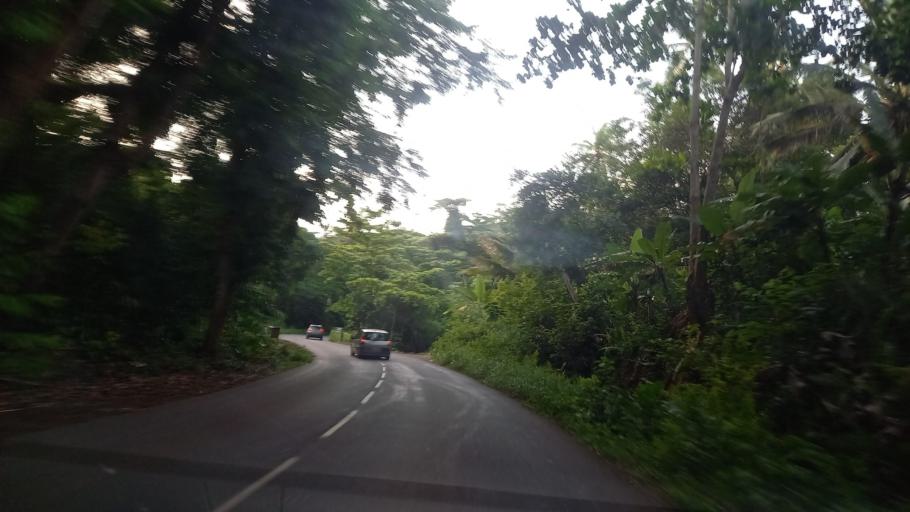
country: YT
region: M'Tsangamouji
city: M'Tsangamouji
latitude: -12.7607
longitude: 45.0986
